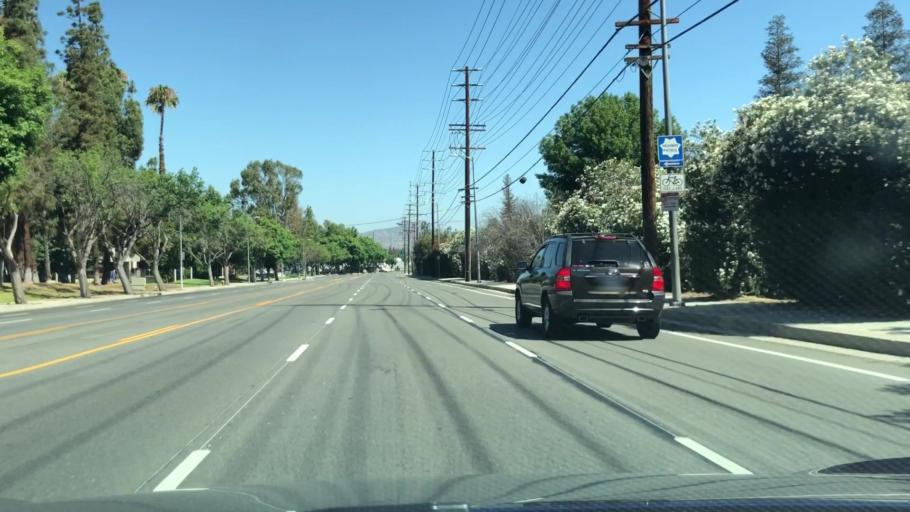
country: US
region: California
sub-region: Los Angeles County
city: Woodland Hills
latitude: 34.1762
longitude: -118.5892
